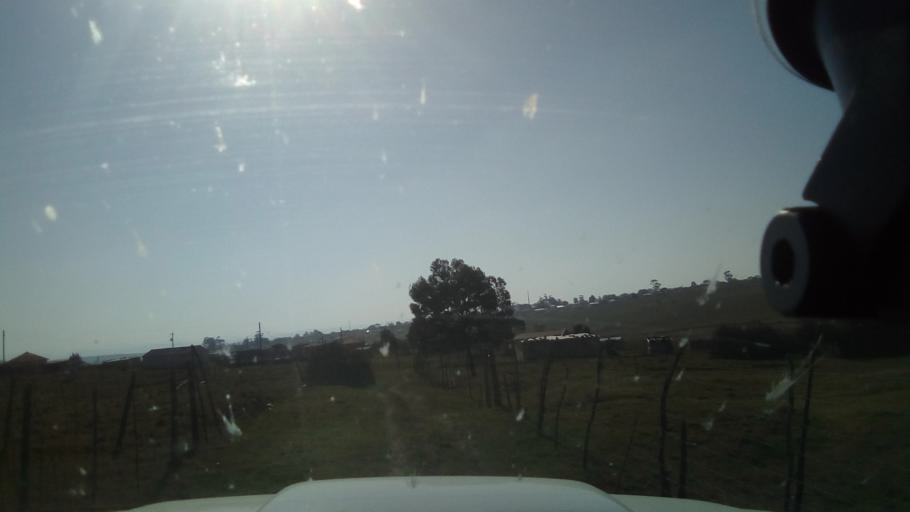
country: ZA
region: Eastern Cape
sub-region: Buffalo City Metropolitan Municipality
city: Bhisho
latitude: -32.9496
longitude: 27.3241
